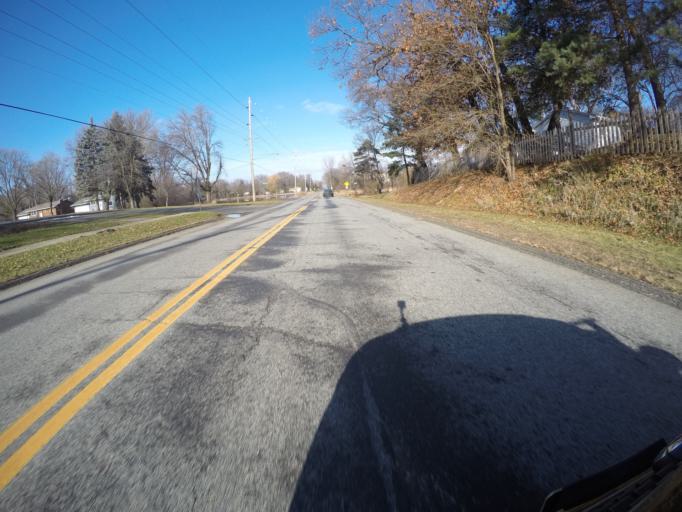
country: US
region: Minnesota
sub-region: Hennepin County
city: Eden Prairie
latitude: 44.8763
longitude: -93.4956
